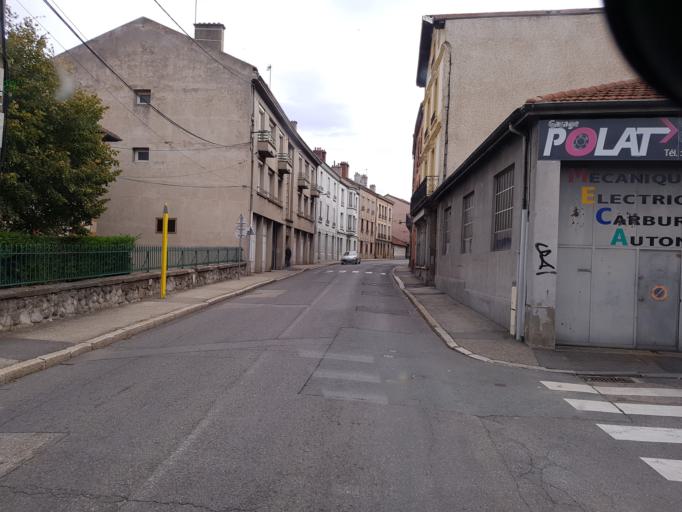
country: FR
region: Rhone-Alpes
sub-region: Departement de la Loire
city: Firminy
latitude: 45.3912
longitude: 4.2921
